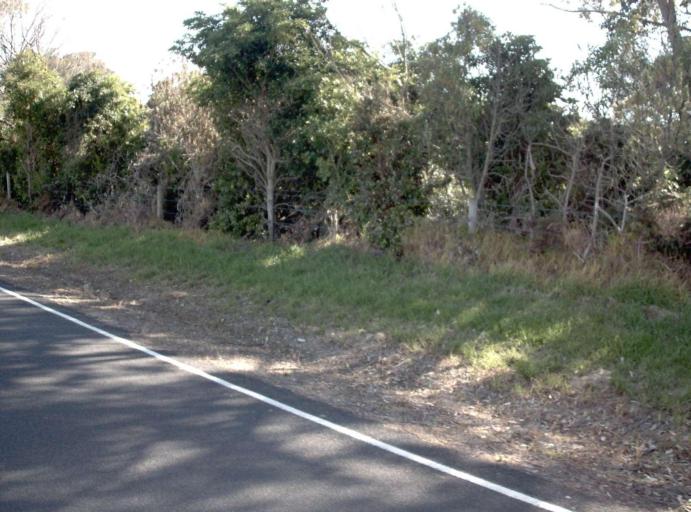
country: AU
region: Victoria
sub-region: East Gippsland
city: Lakes Entrance
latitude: -37.7468
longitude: 148.5167
